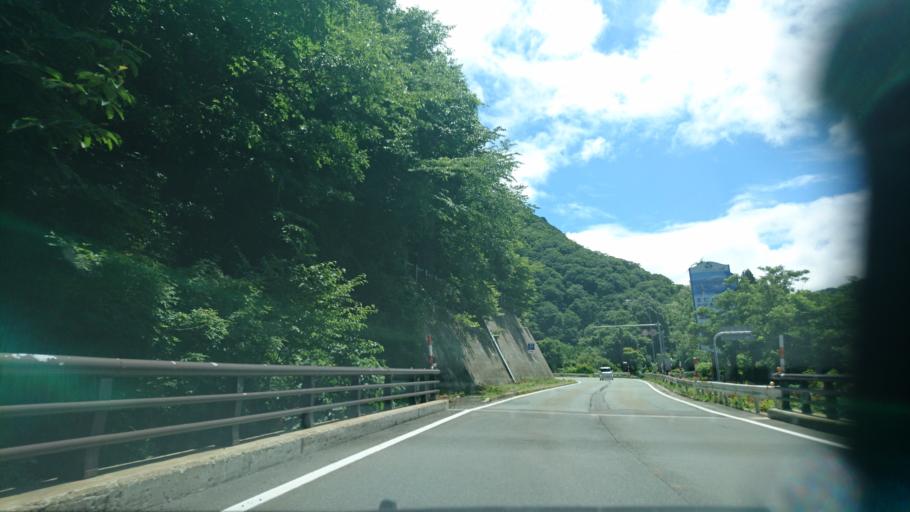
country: JP
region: Iwate
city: Shizukuishi
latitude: 39.6938
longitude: 140.7813
